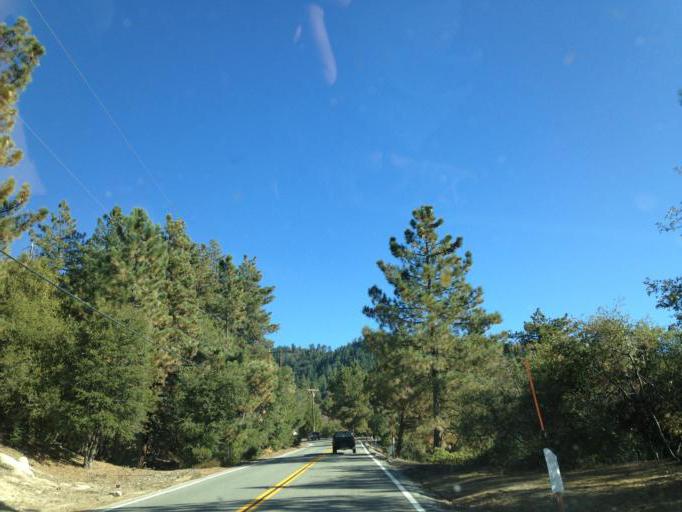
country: US
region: California
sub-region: Riverside County
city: Idyllwild-Pine Cove
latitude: 33.7794
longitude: -116.7449
